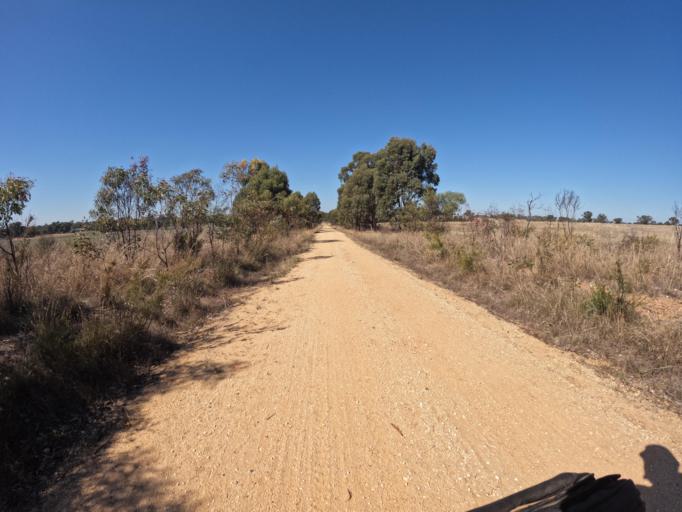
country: AU
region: Victoria
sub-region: Greater Bendigo
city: Kennington
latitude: -36.8218
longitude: 144.5791
